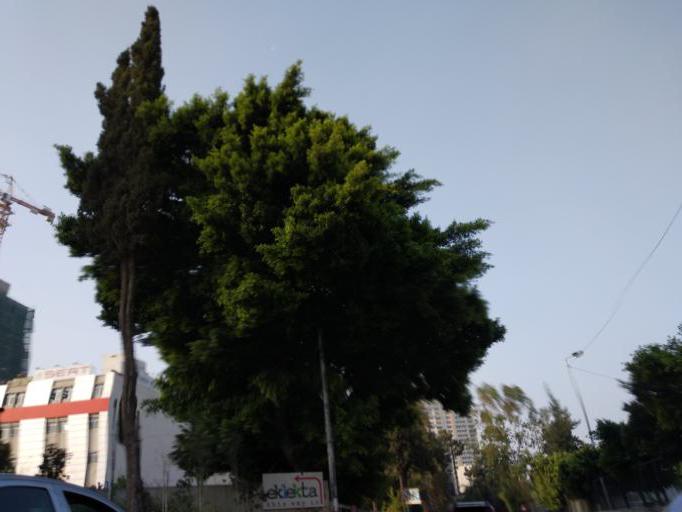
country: LB
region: Beyrouth
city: Beirut
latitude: 33.8826
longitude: 35.5297
